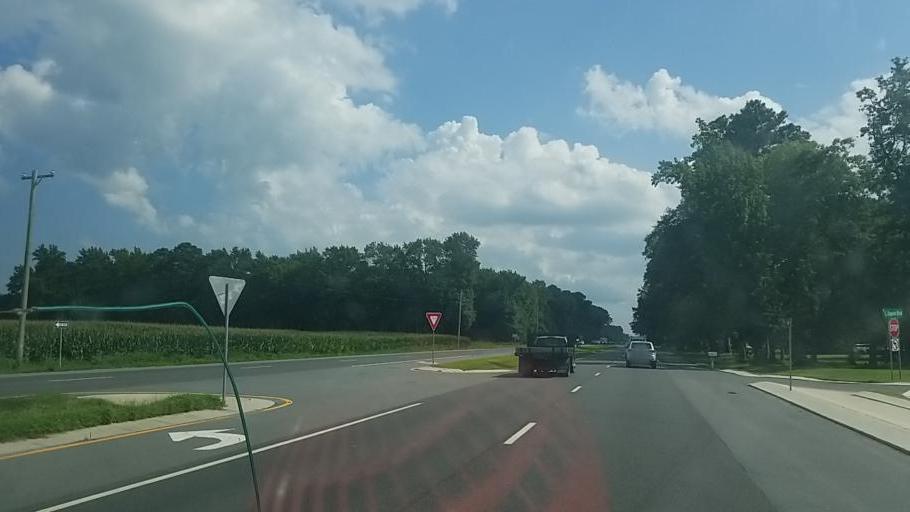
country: US
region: Delaware
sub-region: Sussex County
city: Selbyville
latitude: 38.4748
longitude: -75.2351
